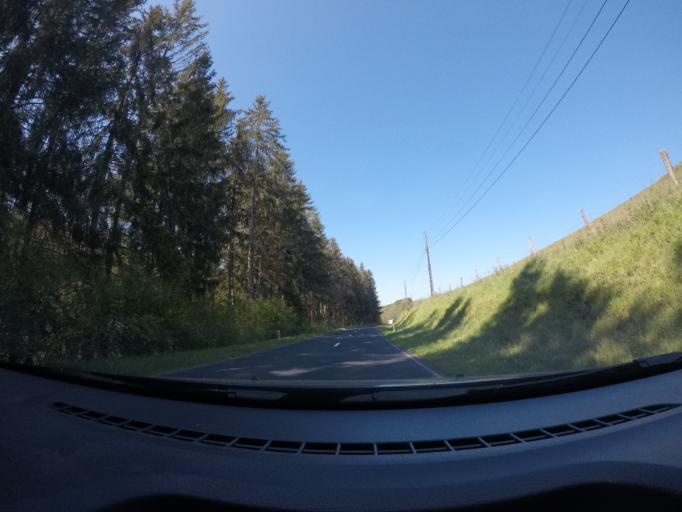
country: BE
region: Wallonia
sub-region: Province du Luxembourg
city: Fauvillers
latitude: 49.8508
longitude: 5.6893
